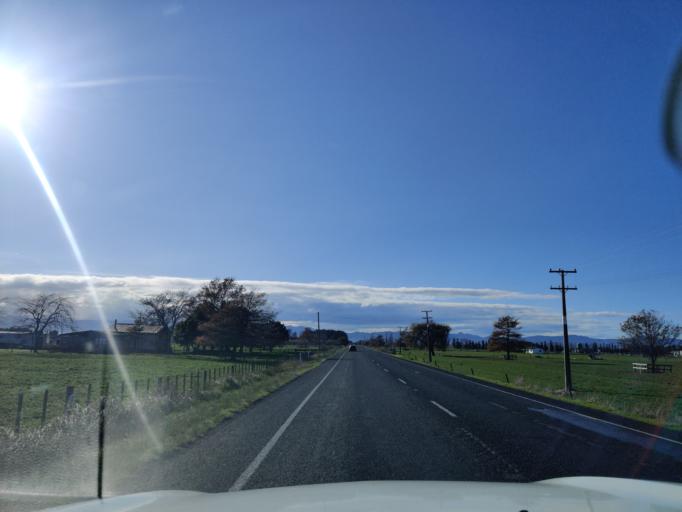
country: NZ
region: Waikato
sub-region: Hauraki District
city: Ngatea
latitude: -37.2740
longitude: 175.5105
